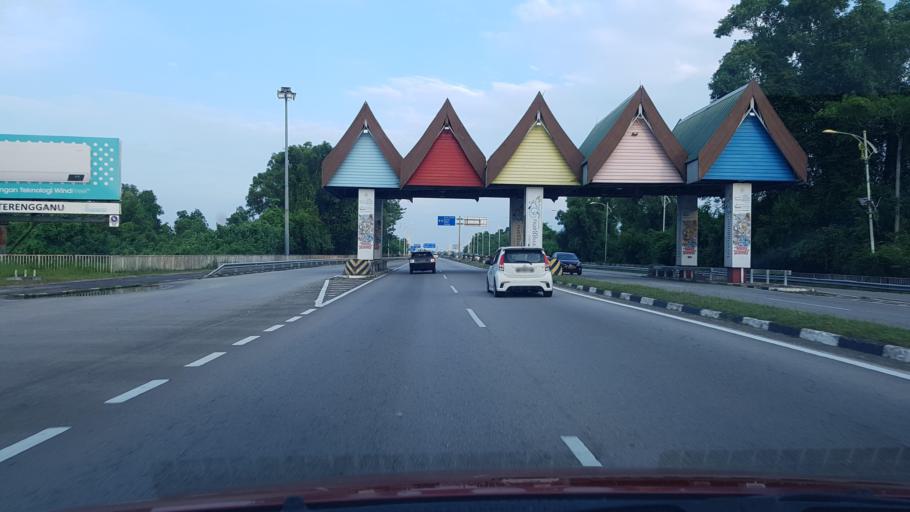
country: MY
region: Terengganu
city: Kuala Terengganu
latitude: 5.3332
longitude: 103.1177
